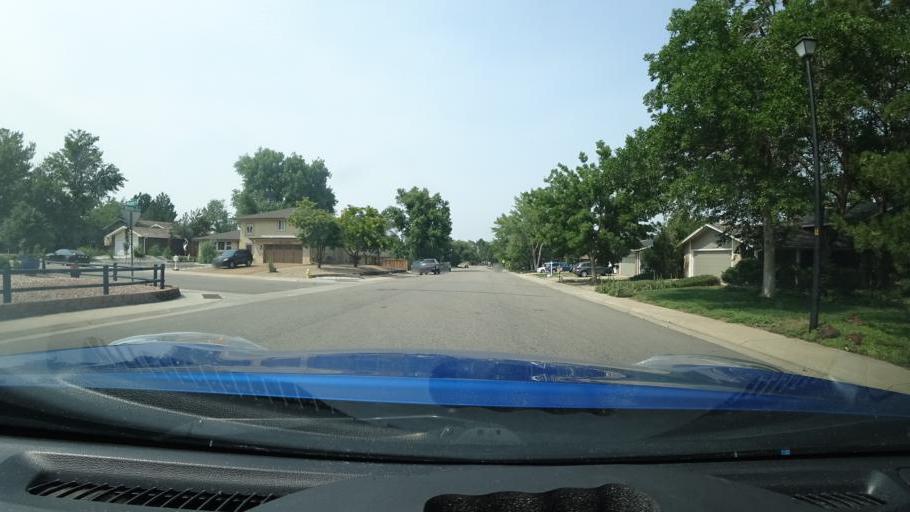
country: US
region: Colorado
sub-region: Adams County
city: Aurora
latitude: 39.6704
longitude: -104.8525
